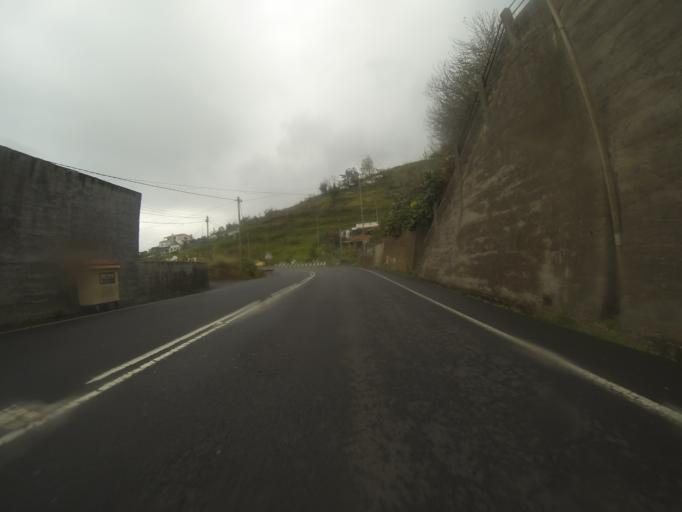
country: PT
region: Madeira
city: Canico
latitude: 32.6481
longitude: -16.8664
